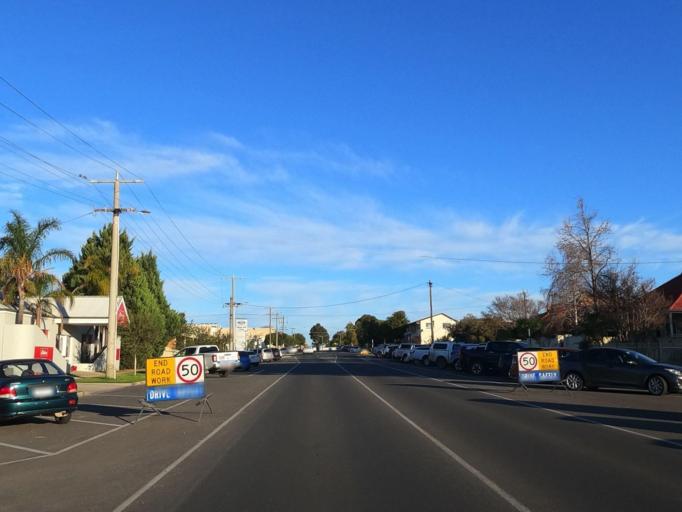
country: AU
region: Victoria
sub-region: Swan Hill
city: Swan Hill
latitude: -35.3356
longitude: 143.5571
